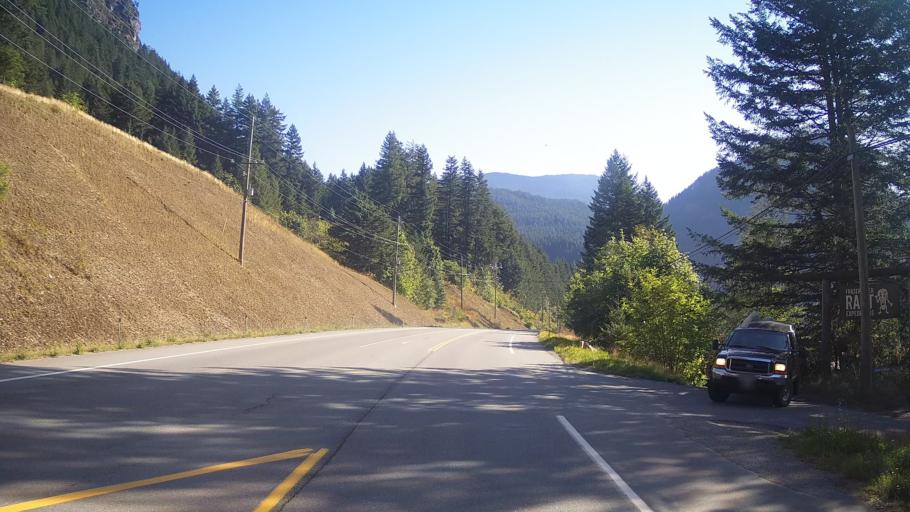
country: CA
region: British Columbia
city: Hope
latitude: 49.5592
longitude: -121.4426
